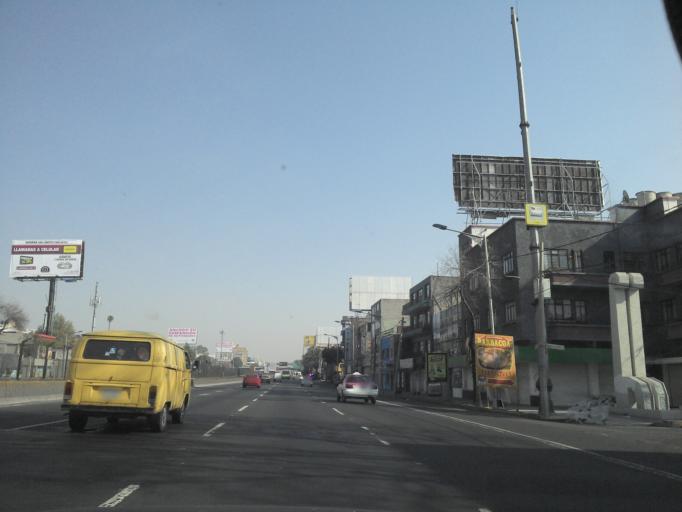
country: MX
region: Mexico City
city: Colonia Nativitas
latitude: 19.3904
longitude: -99.1384
